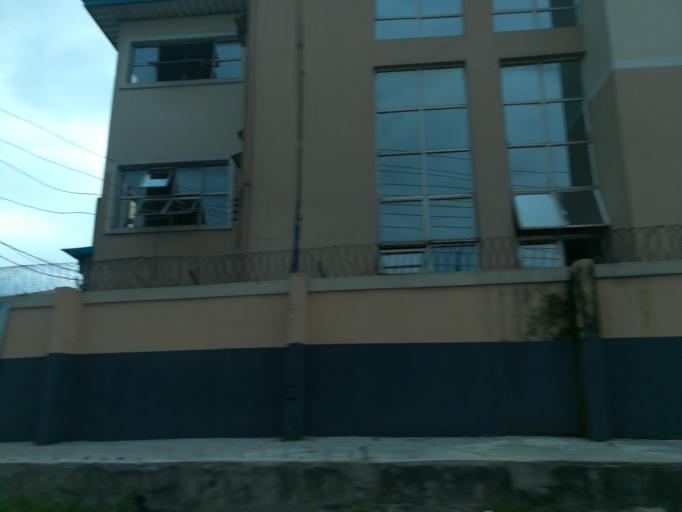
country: NG
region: Rivers
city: Port Harcourt
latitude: 4.7989
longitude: 6.9861
